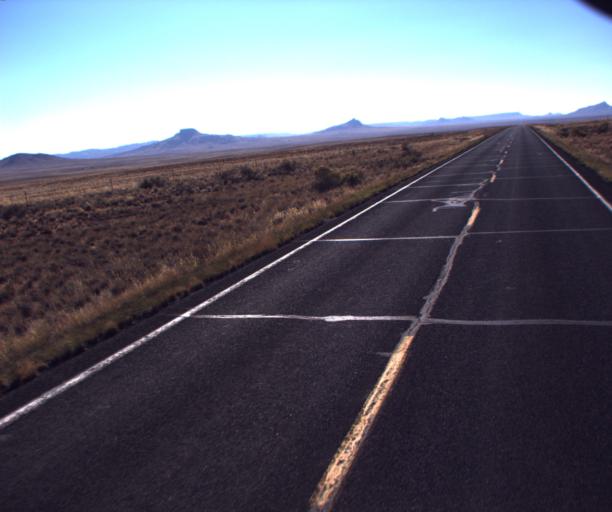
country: US
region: Arizona
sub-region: Navajo County
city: First Mesa
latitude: 35.6356
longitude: -110.4838
